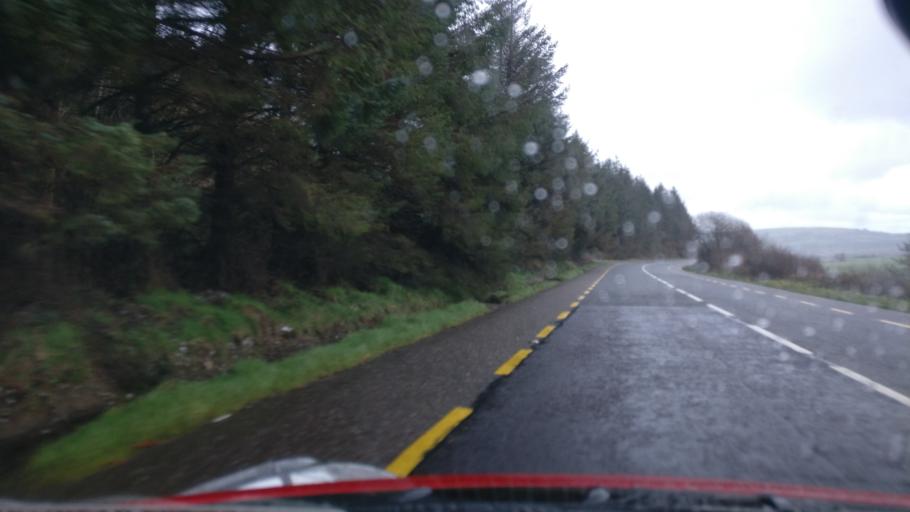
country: IE
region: Munster
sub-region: Ciarrai
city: Castleisland
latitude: 52.2976
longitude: -9.3882
